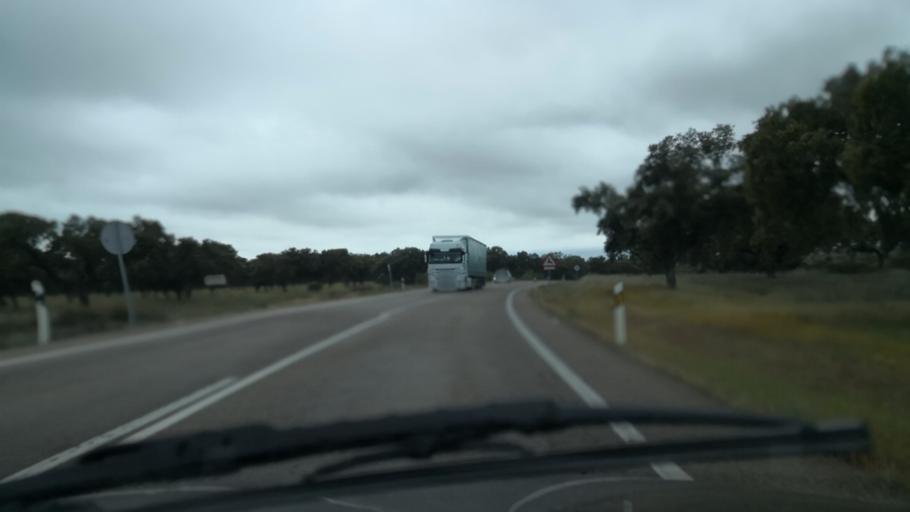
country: ES
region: Extremadura
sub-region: Provincia de Badajoz
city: Villar del Rey
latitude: 39.0410
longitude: -6.8100
